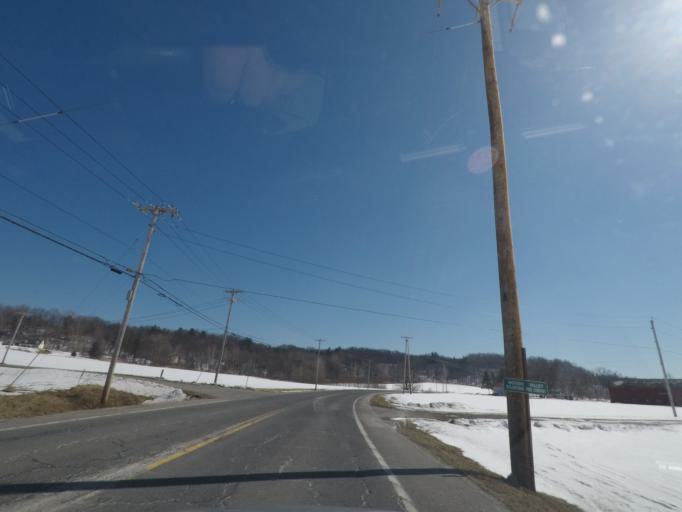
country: US
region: New York
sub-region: Saratoga County
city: Stillwater
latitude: 42.9227
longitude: -73.6333
